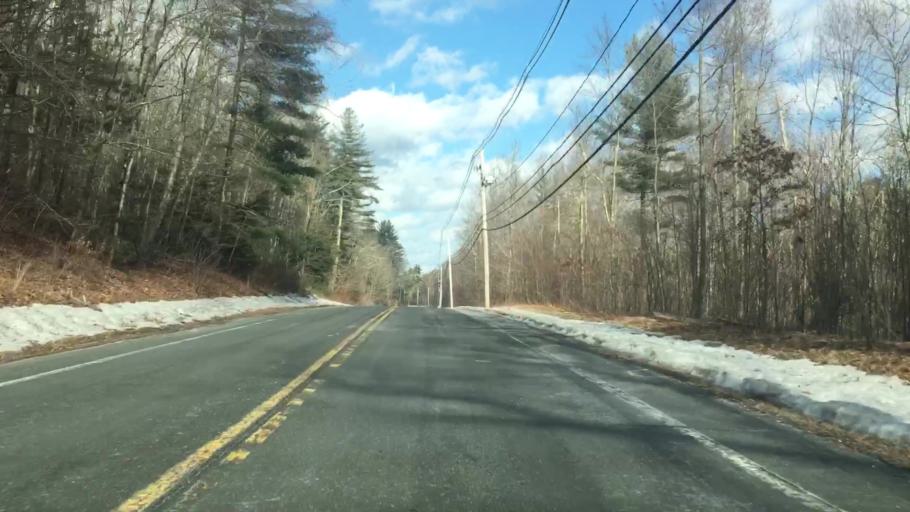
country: US
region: Massachusetts
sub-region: Hampden County
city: Wales
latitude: 42.0837
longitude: -72.2005
